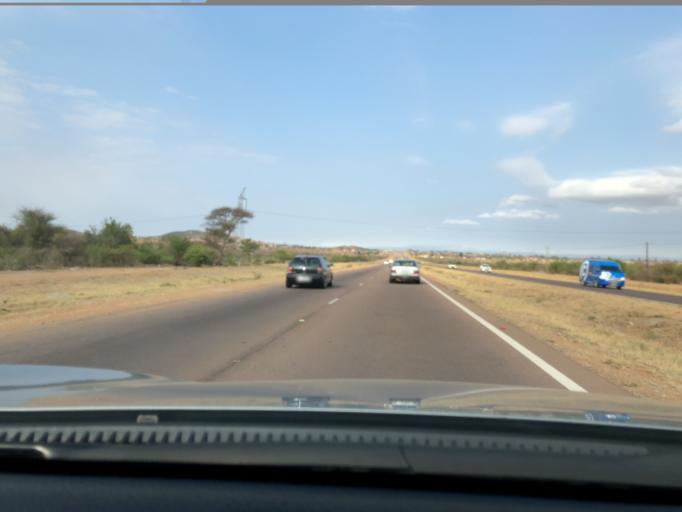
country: ZA
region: Limpopo
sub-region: Capricorn District Municipality
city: Polokwane
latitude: -23.8948
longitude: 29.6359
